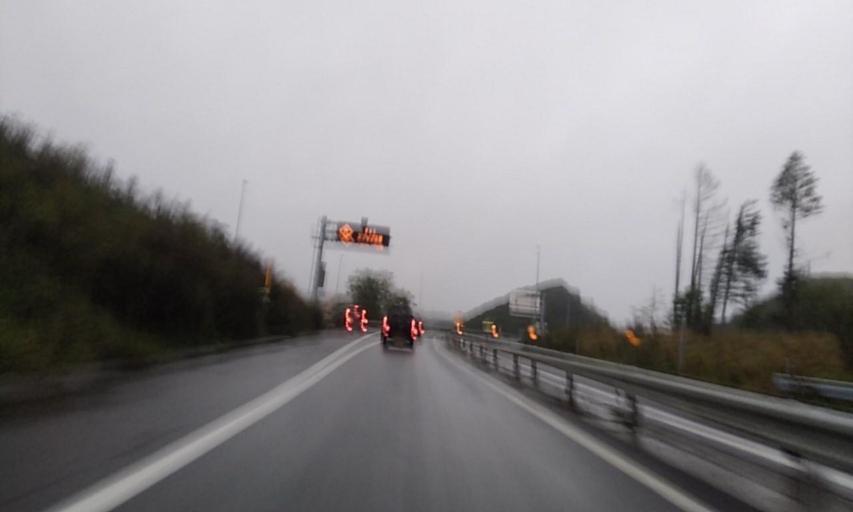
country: JP
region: Hokkaido
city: Kushiro
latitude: 43.0055
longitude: 144.5033
